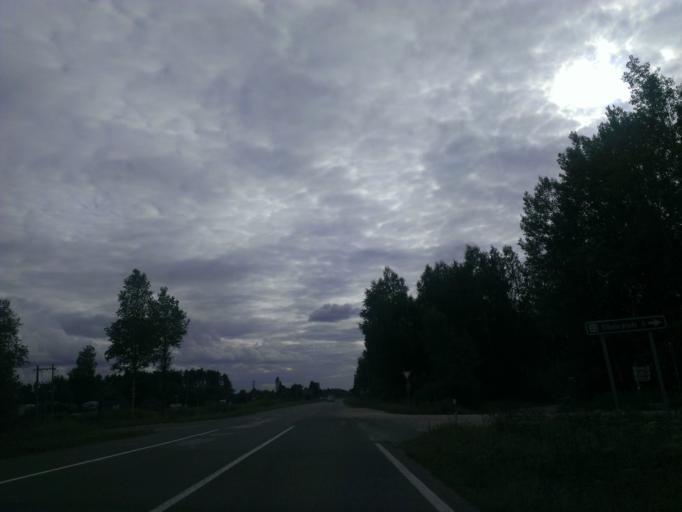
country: LV
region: Incukalns
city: Vangazi
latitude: 57.0932
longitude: 24.5629
